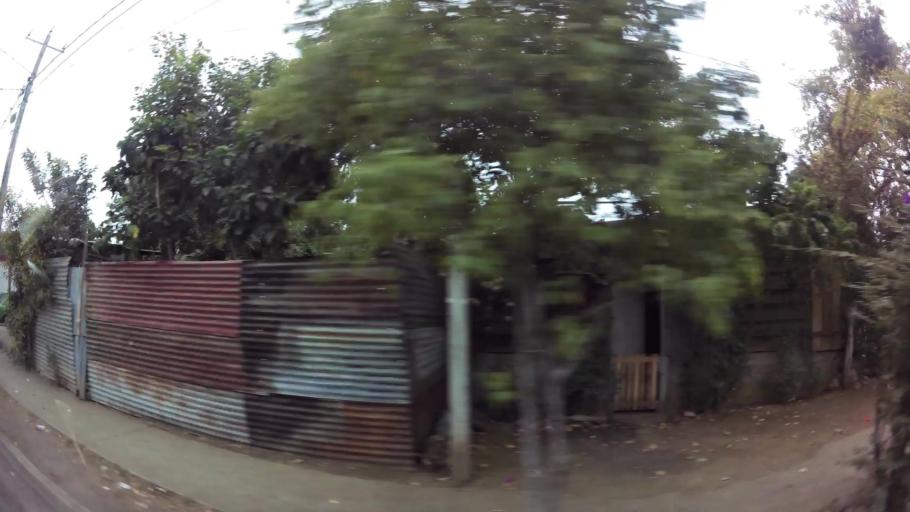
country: NI
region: Managua
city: Managua
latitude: 12.1090
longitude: -86.2314
